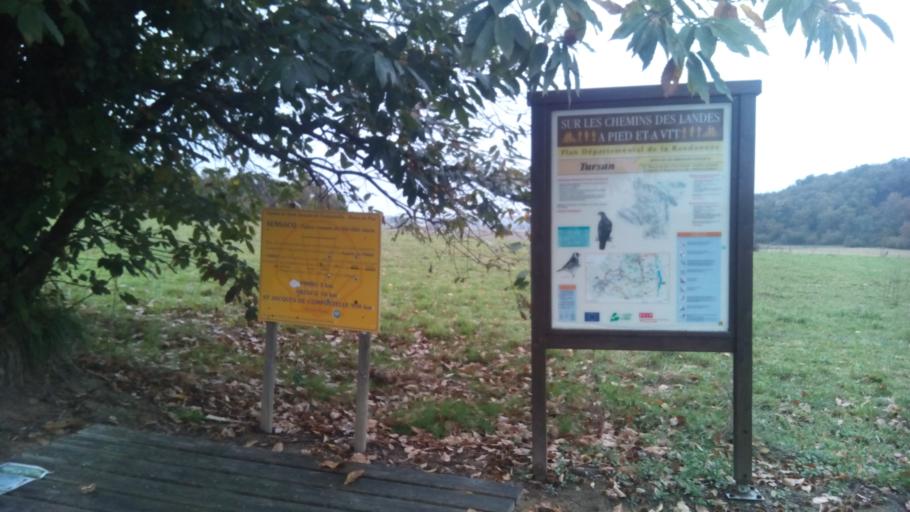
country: FR
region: Aquitaine
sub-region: Departement des Pyrenees-Atlantiques
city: Garlin
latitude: 43.5829
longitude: -0.3493
